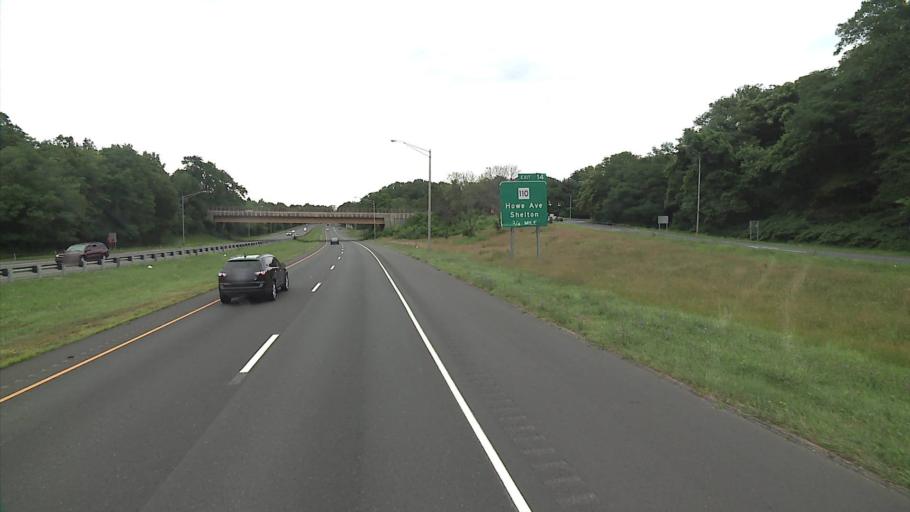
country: US
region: Connecticut
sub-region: Fairfield County
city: Shelton
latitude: 41.3032
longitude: -73.1000
